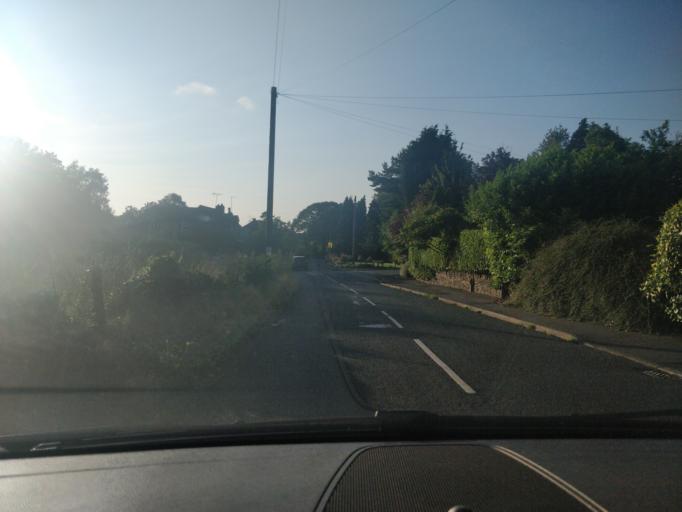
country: GB
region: England
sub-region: Lancashire
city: Parbold
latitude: 53.5737
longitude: -2.7655
